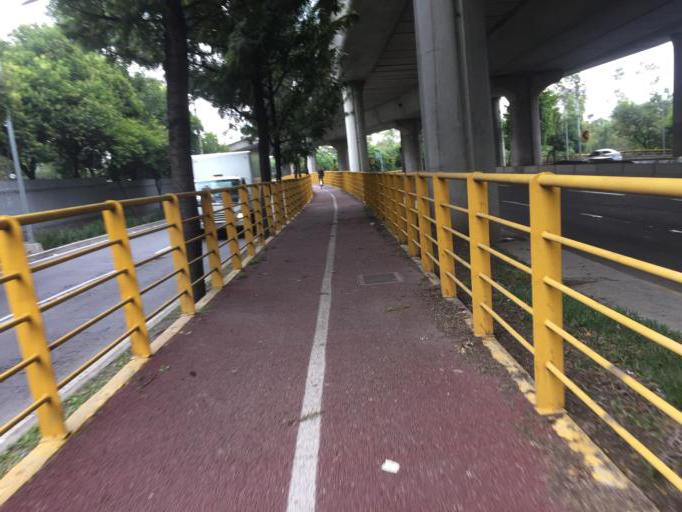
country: MX
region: Mexico City
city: Polanco
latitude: 19.4135
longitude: -99.1937
